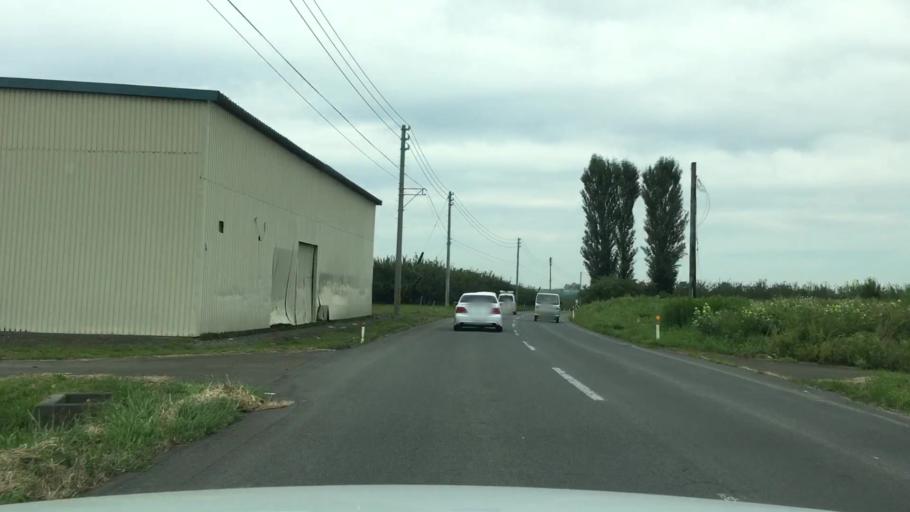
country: JP
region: Aomori
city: Hirosaki
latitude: 40.6462
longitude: 140.4241
